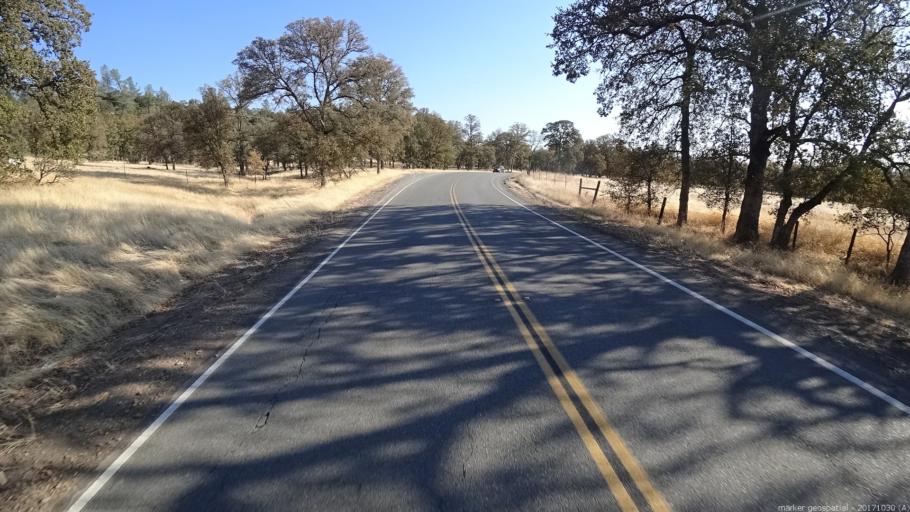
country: US
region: California
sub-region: Shasta County
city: Palo Cedro
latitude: 40.5673
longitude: -122.2044
